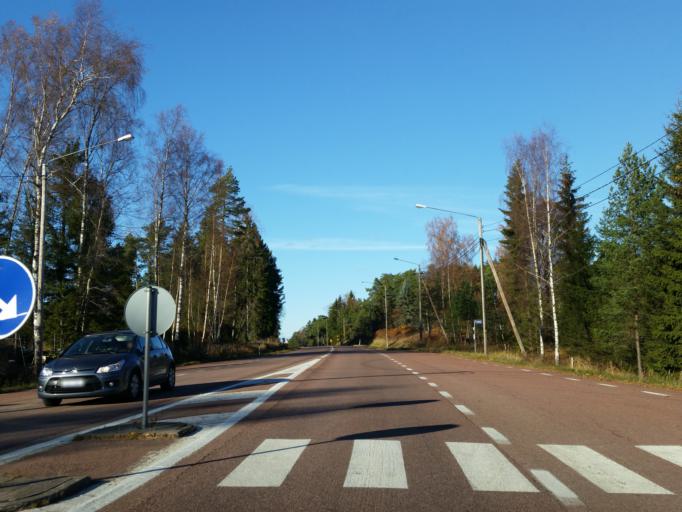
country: AX
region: Alands landsbygd
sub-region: Finstroem
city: Finstroem
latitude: 60.2343
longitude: 19.9814
